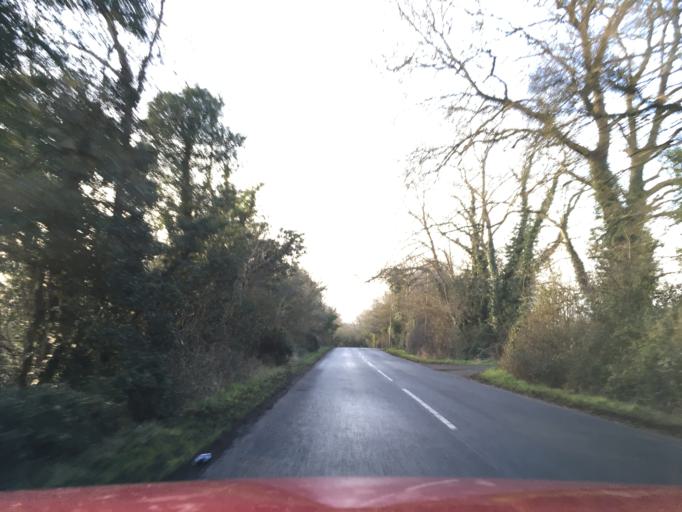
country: GB
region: England
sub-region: Warwickshire
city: Henley in Arden
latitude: 52.2457
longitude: -1.7746
